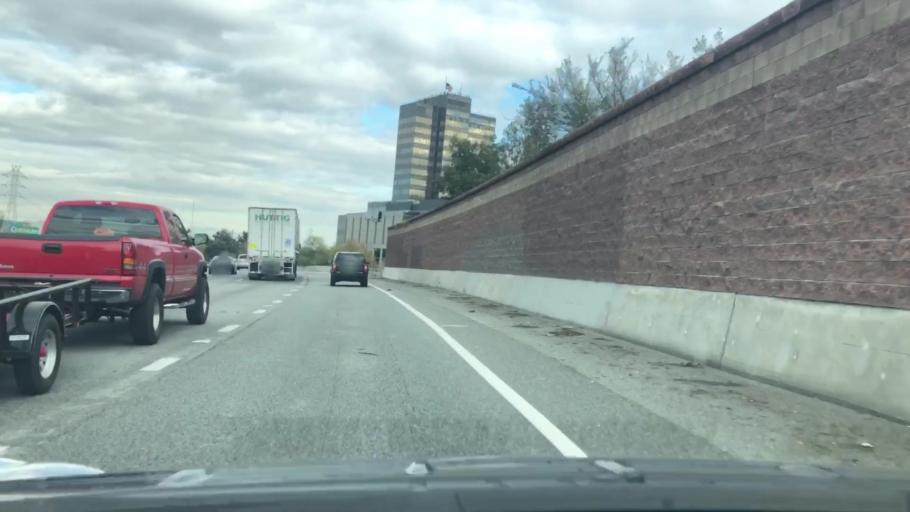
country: US
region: California
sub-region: Santa Clara County
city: Campbell
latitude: 37.2870
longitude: -121.9306
